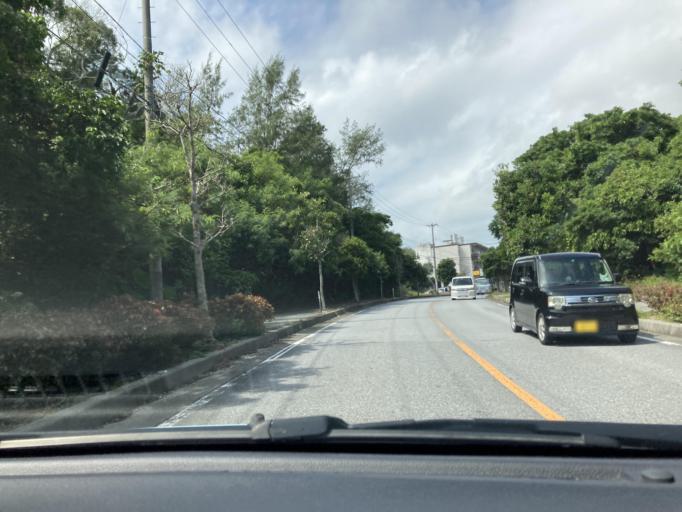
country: JP
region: Okinawa
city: Ishikawa
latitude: 26.4044
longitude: 127.8404
